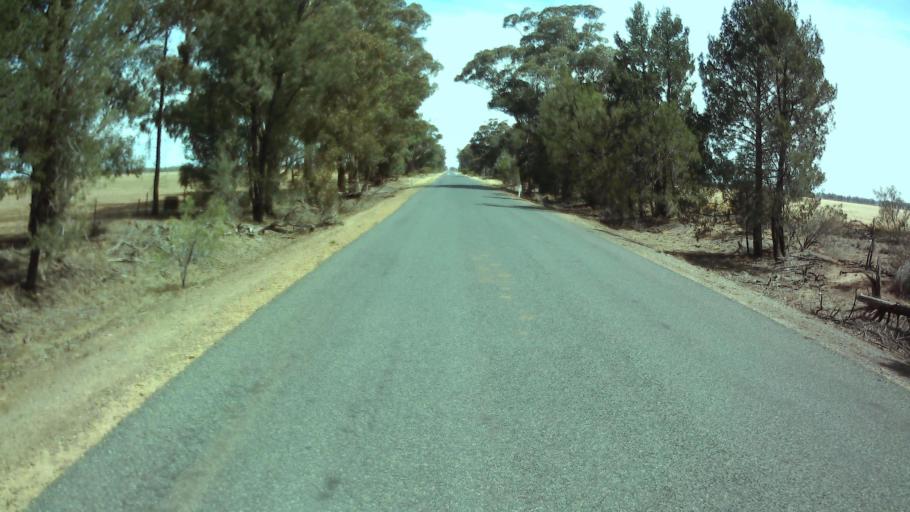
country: AU
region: New South Wales
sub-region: Weddin
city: Grenfell
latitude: -33.9756
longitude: 147.7790
